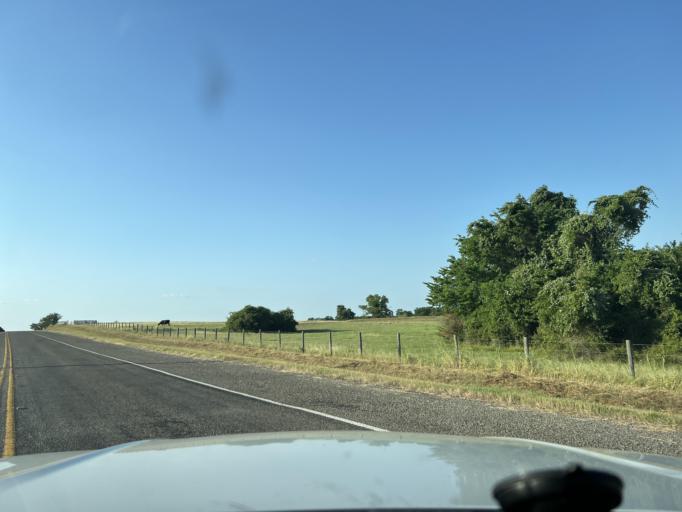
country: US
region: Texas
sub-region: Washington County
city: Brenham
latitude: 30.1809
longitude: -96.3939
